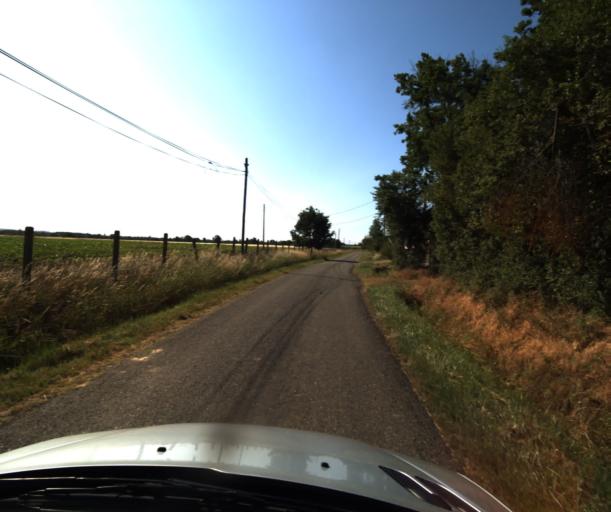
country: FR
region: Midi-Pyrenees
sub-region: Departement du Tarn-et-Garonne
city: Bressols
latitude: 43.9654
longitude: 1.2867
